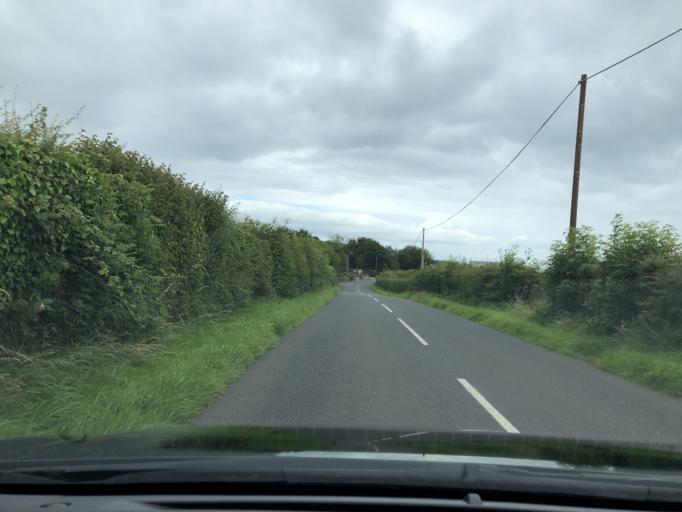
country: GB
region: Northern Ireland
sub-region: Larne District
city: Larne
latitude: 54.8419
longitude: -5.8366
